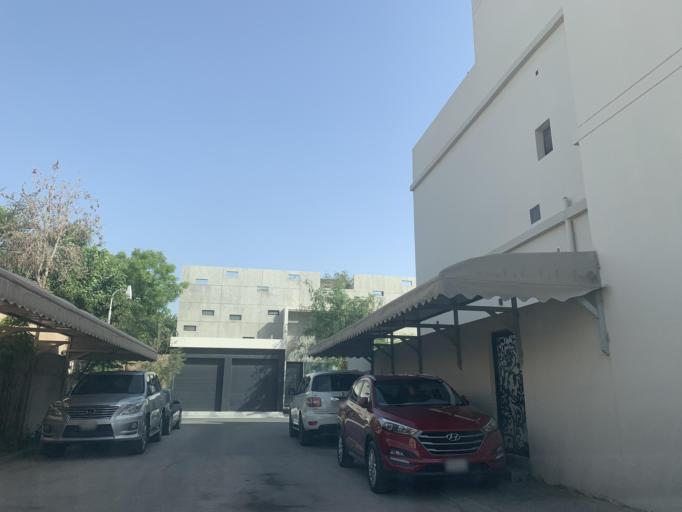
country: BH
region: Northern
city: Madinat `Isa
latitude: 26.1670
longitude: 50.5704
